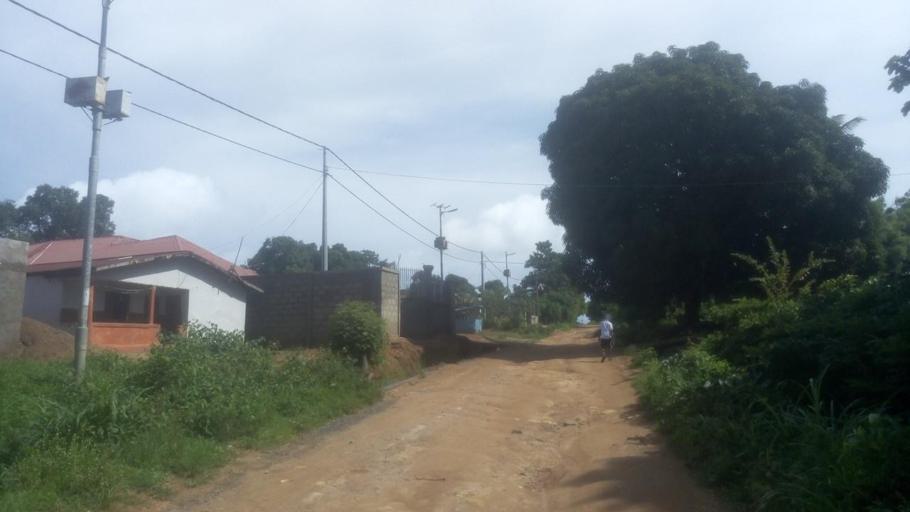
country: SL
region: Northern Province
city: Masoyila
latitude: 8.6094
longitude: -13.1955
